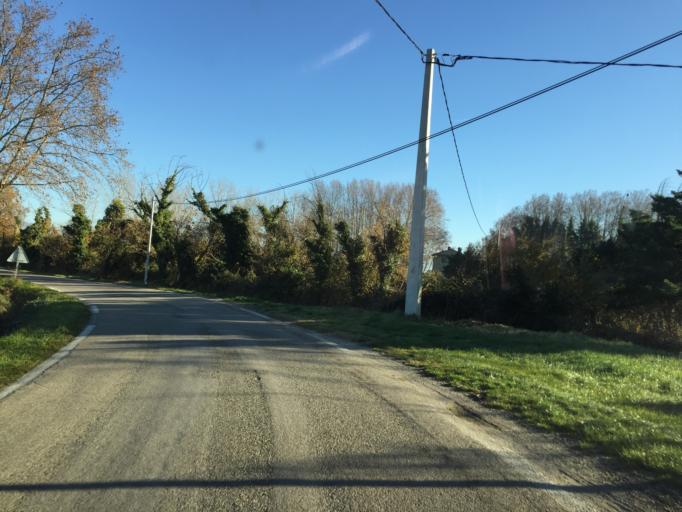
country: FR
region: Provence-Alpes-Cote d'Azur
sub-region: Departement du Vaucluse
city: Sarrians
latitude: 44.0661
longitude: 4.9415
